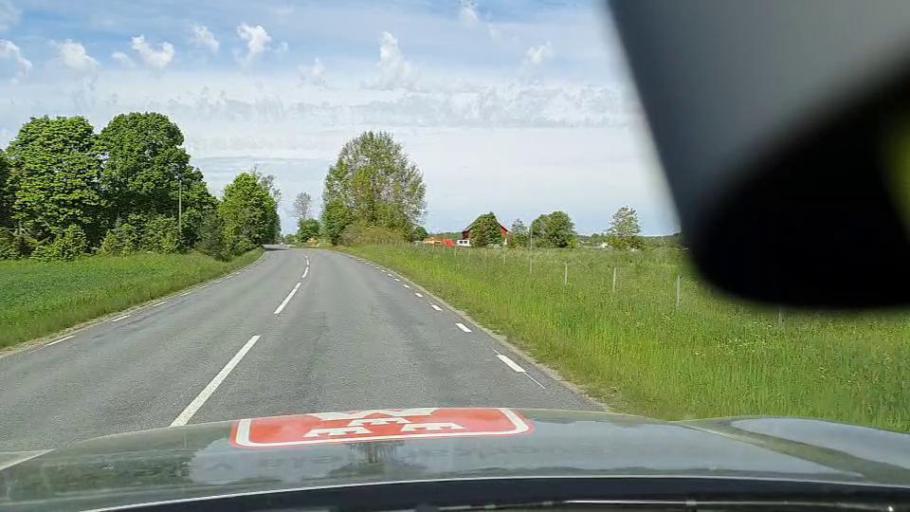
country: SE
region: Soedermanland
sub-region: Eskilstuna Kommun
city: Skogstorp
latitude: 59.3063
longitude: 16.4628
